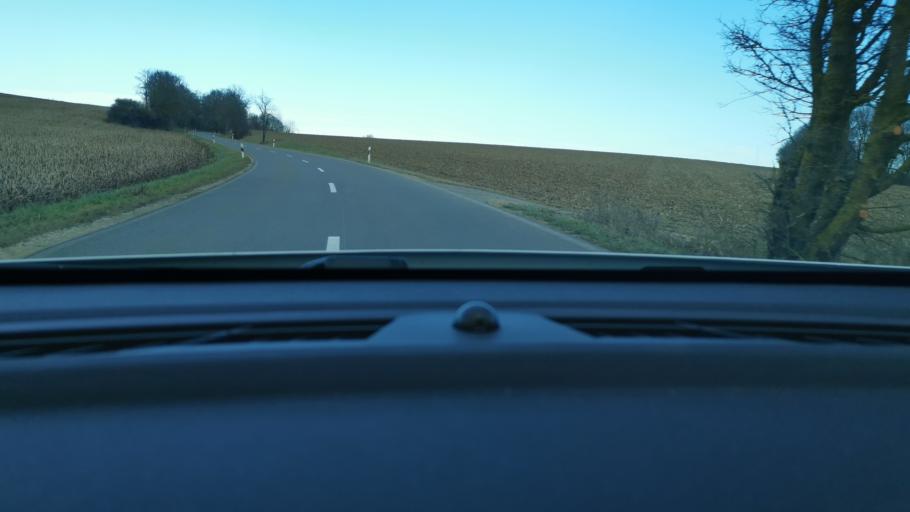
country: DE
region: Bavaria
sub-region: Swabia
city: Affing
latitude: 48.4892
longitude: 10.9736
